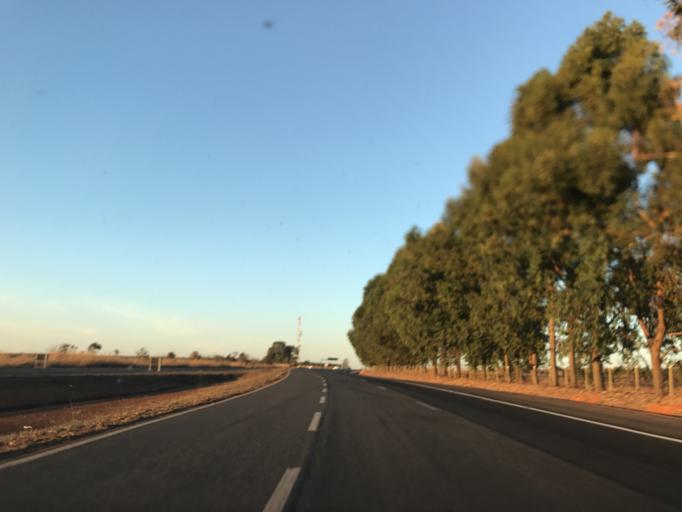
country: BR
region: Goias
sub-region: Abadiania
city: Abadiania
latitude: -16.2087
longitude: -48.7431
